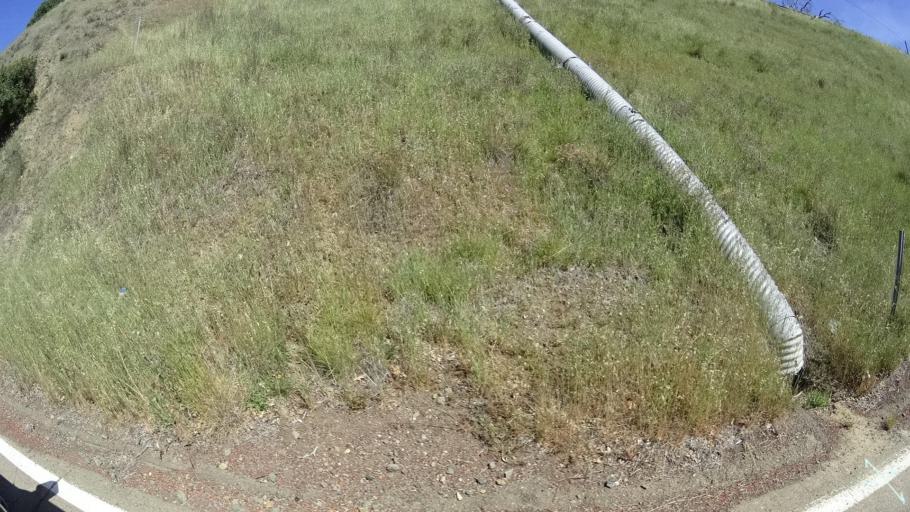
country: US
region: California
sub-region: Lake County
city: Cobb
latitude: 38.7838
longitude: -122.7153
